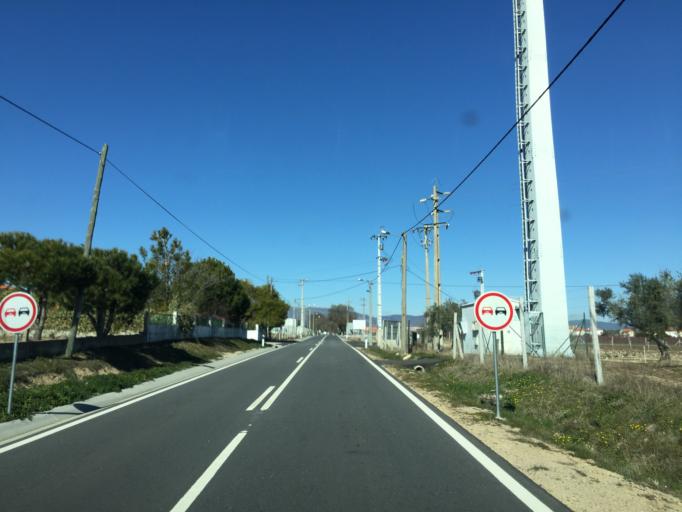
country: PT
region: Guarda
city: Alcains
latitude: 39.9817
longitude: -7.4574
